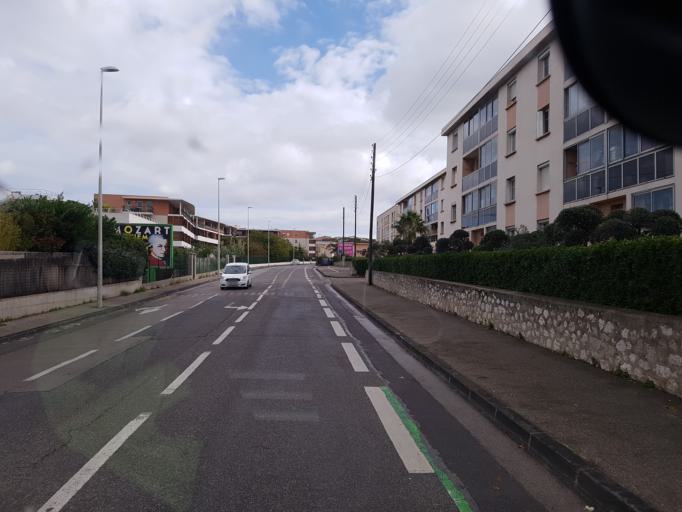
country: FR
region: Provence-Alpes-Cote d'Azur
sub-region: Departement des Bouches-du-Rhone
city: Marseille 09
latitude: 43.2468
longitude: 5.3839
